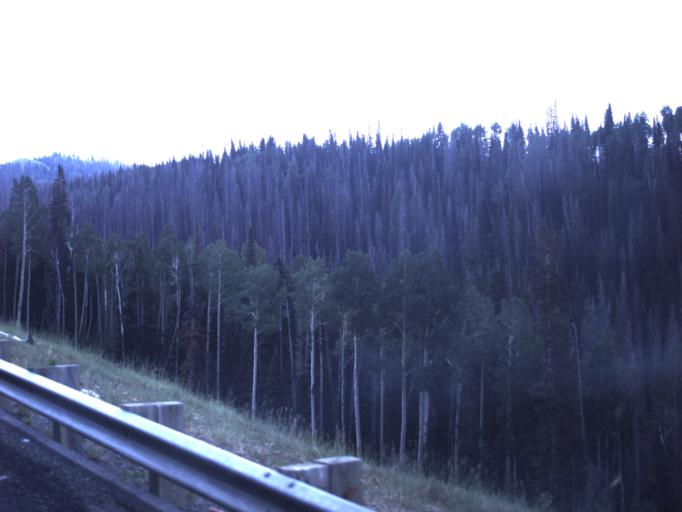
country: US
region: Utah
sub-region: Summit County
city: Francis
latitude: 40.5040
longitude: -111.0441
